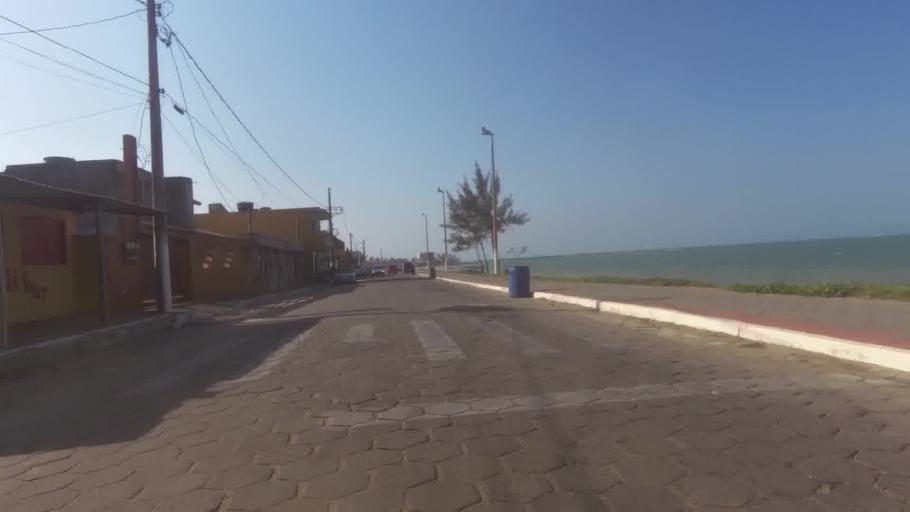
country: BR
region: Espirito Santo
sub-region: Itapemirim
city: Itapemirim
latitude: -21.0148
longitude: -40.8095
